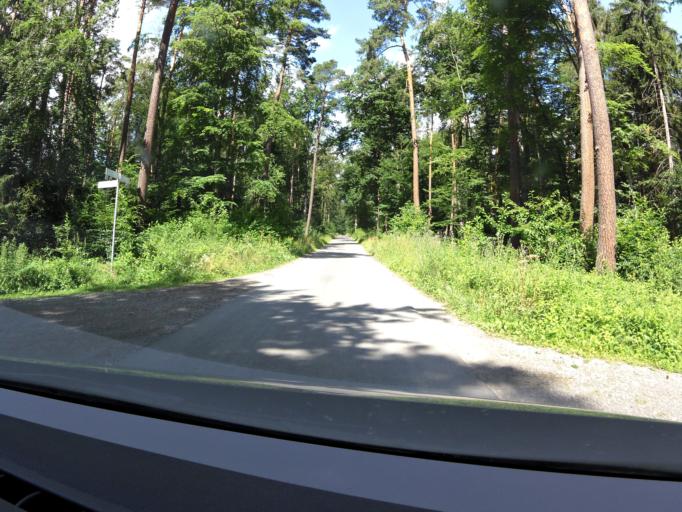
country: DE
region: Baden-Wuerttemberg
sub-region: Tuebingen Region
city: Tuebingen
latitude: 48.5511
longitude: 9.0012
